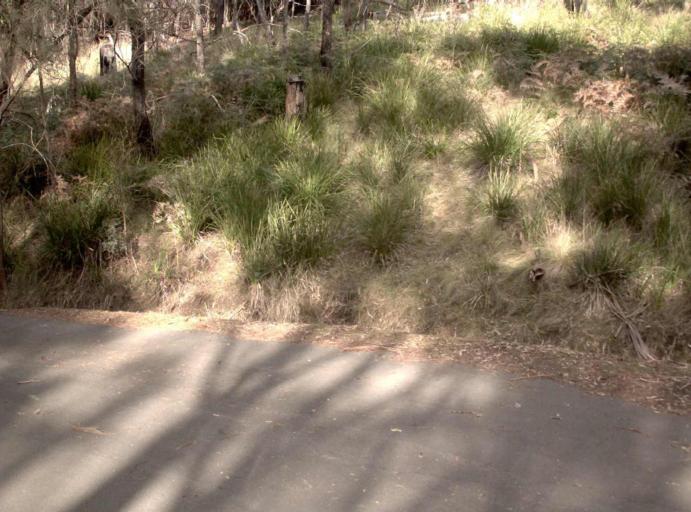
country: AU
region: Tasmania
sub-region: Launceston
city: West Launceston
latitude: -41.4414
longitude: 147.1149
